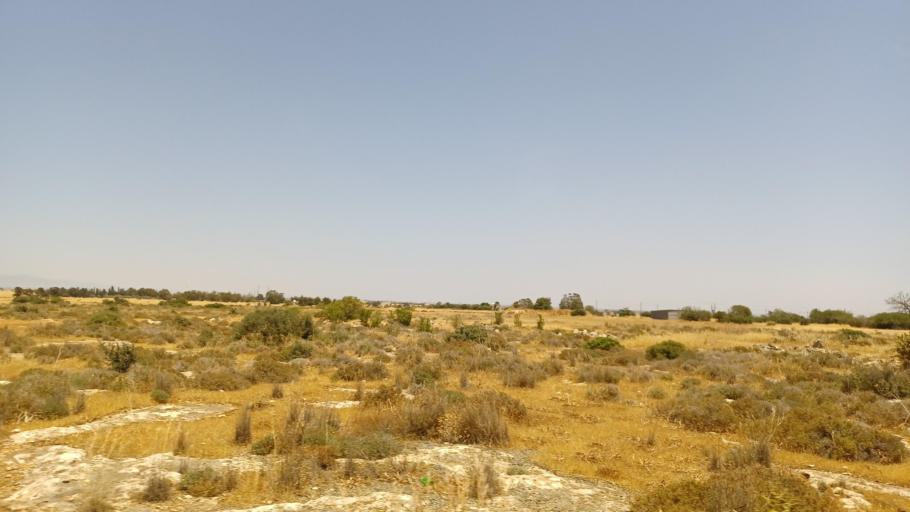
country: CY
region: Larnaka
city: Pergamos
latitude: 35.0249
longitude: 33.7081
